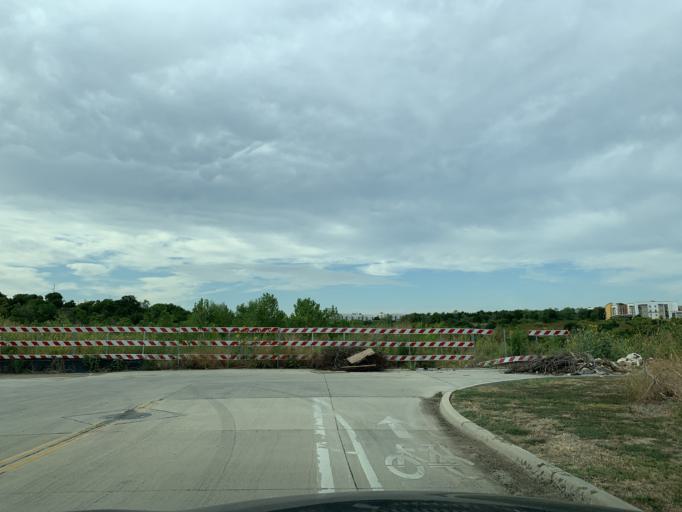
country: US
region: Texas
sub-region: Dallas County
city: Cockrell Hill
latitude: 32.7620
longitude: -96.8759
